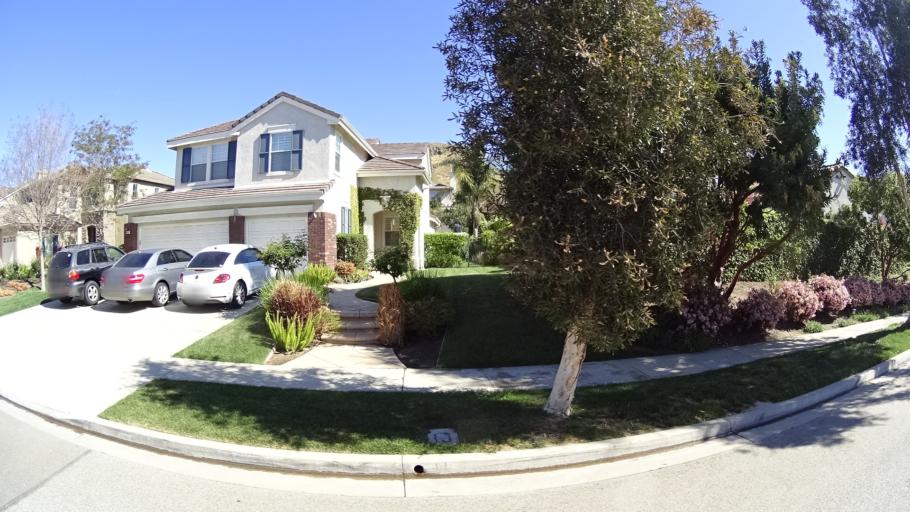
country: US
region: California
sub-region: Ventura County
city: Casa Conejo
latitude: 34.1749
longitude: -118.9788
